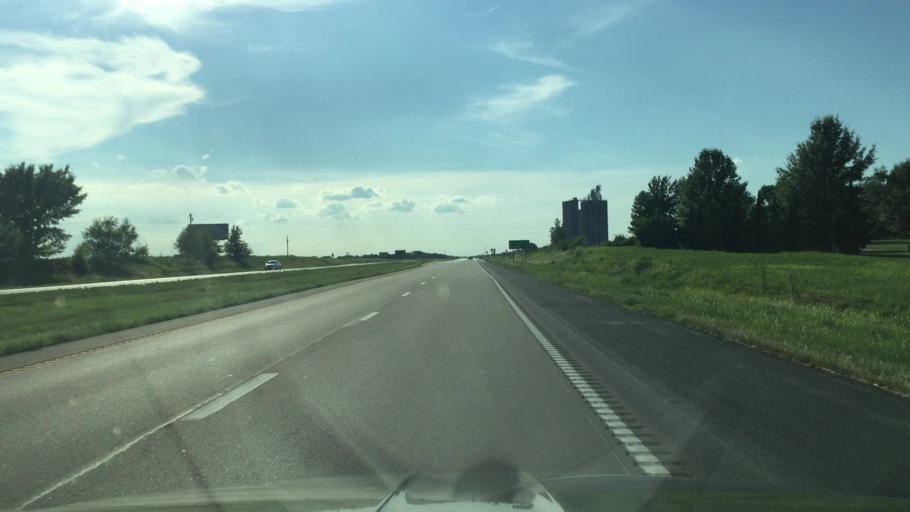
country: US
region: Missouri
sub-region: Pettis County
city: La Monte
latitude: 38.7467
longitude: -93.3379
